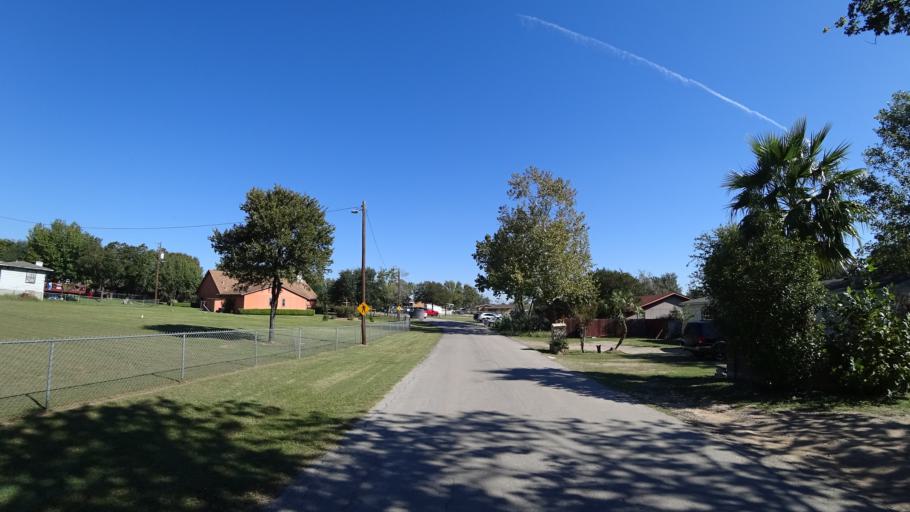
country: US
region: Texas
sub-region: Travis County
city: Hornsby Bend
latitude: 30.2641
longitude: -97.6266
